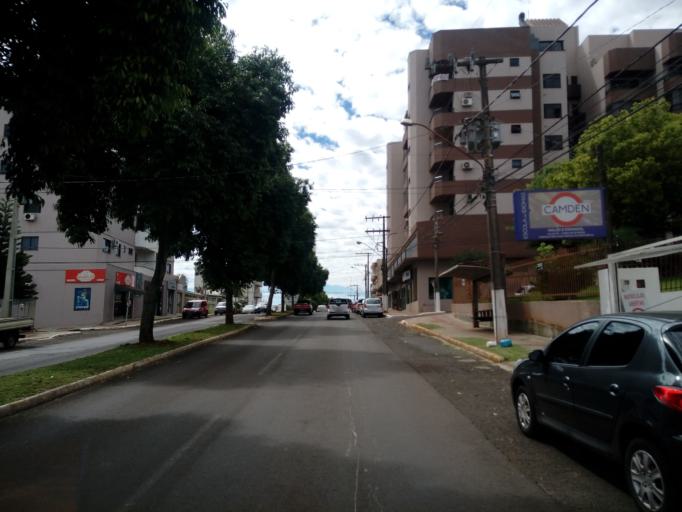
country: BR
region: Santa Catarina
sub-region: Chapeco
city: Chapeco
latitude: -27.0943
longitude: -52.6117
